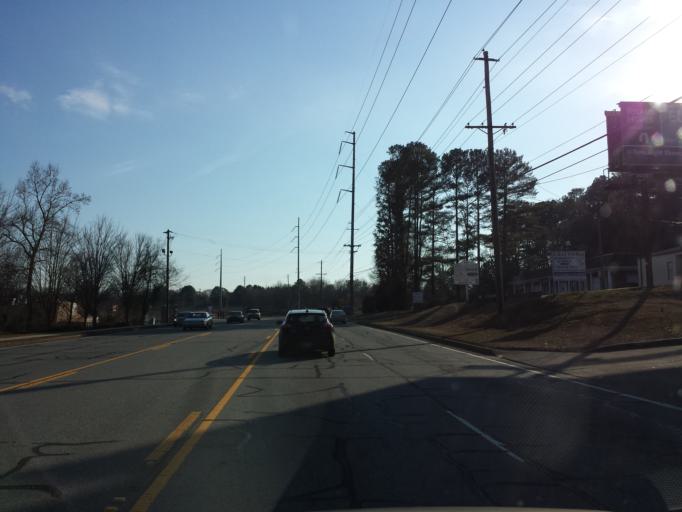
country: US
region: Georgia
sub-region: Cherokee County
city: Woodstock
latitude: 34.0477
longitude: -84.5284
